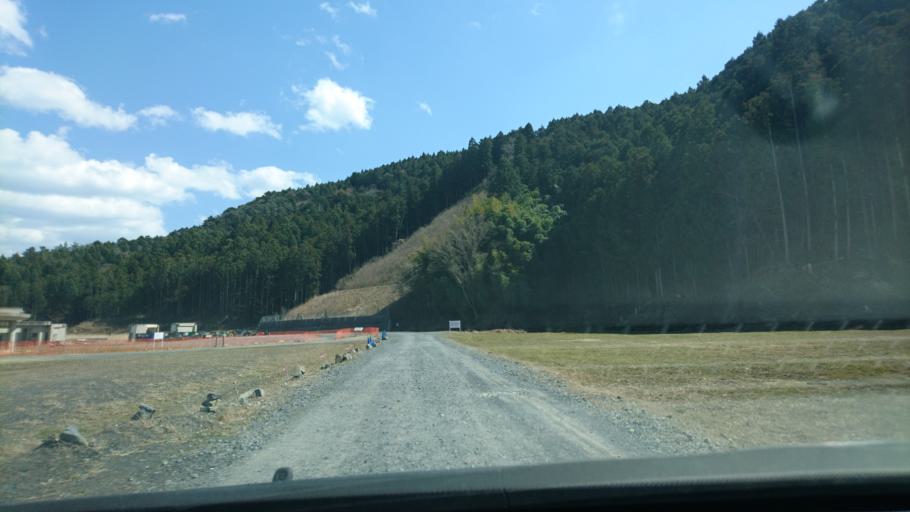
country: JP
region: Miyagi
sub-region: Oshika Gun
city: Onagawa Cho
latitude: 38.5460
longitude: 141.4274
